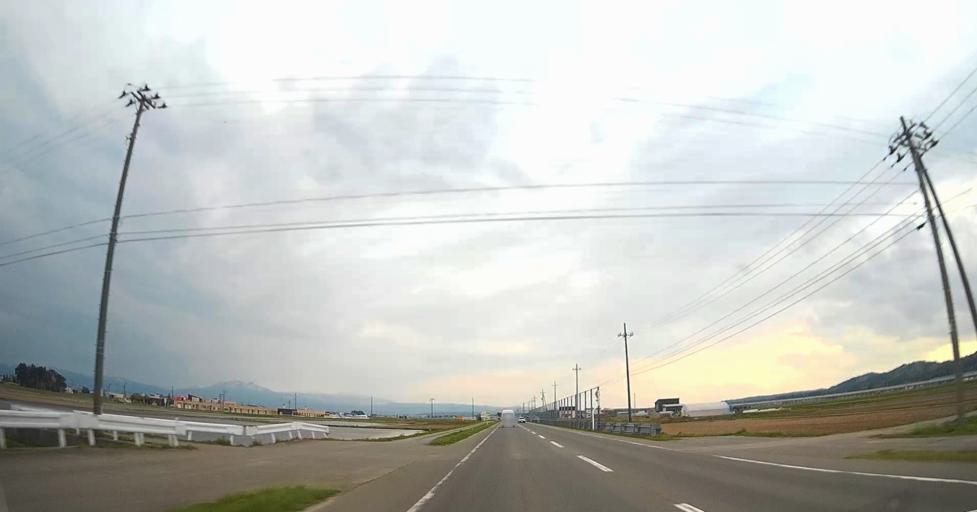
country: JP
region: Aomori
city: Aomori Shi
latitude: 40.8906
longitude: 140.6689
